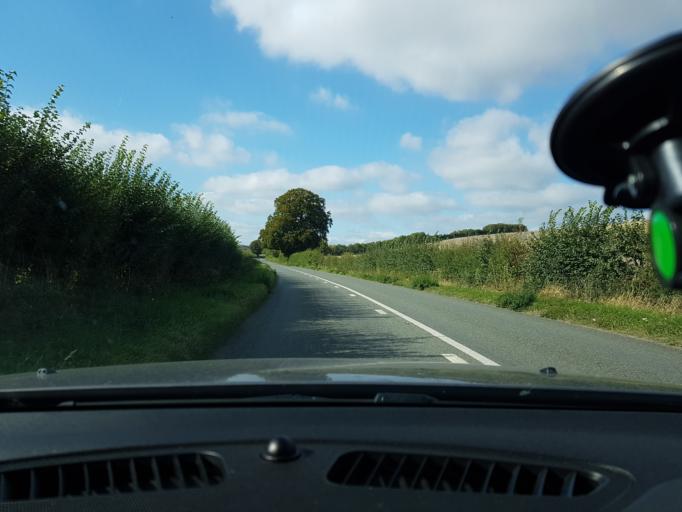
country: GB
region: England
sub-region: Wiltshire
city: Aldbourne
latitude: 51.4875
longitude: -1.6381
